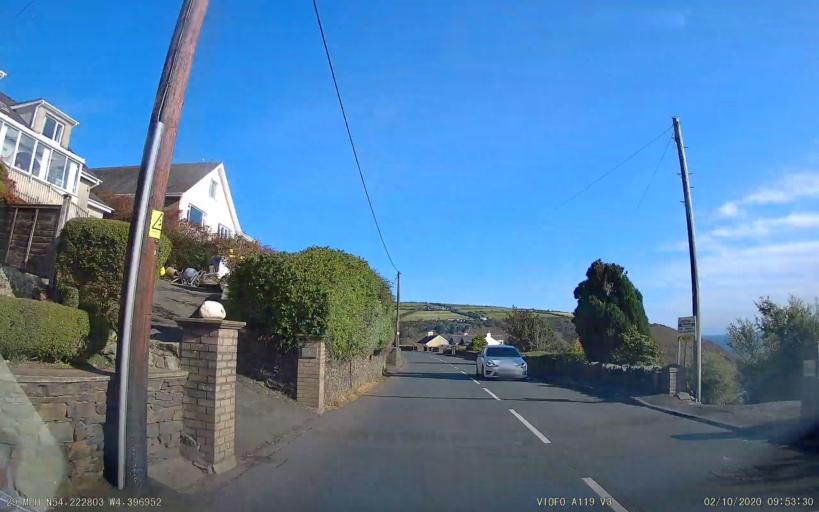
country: IM
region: Laxey
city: Laxey
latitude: 54.2228
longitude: -4.3970
